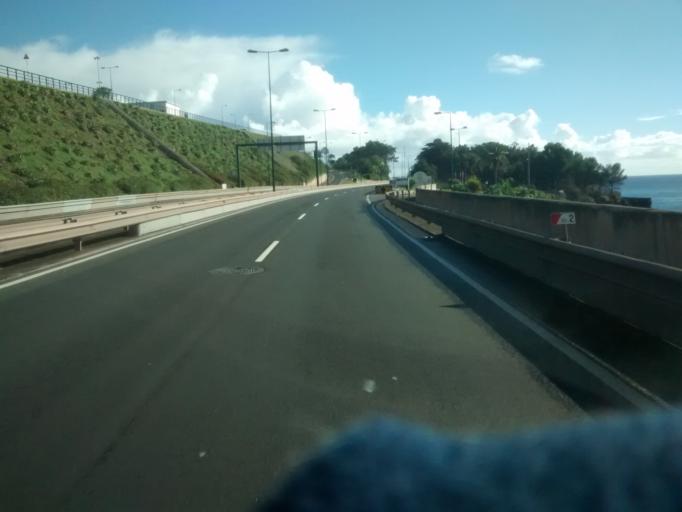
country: PT
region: Madeira
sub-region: Machico
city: Machico
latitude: 32.6899
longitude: -16.7801
